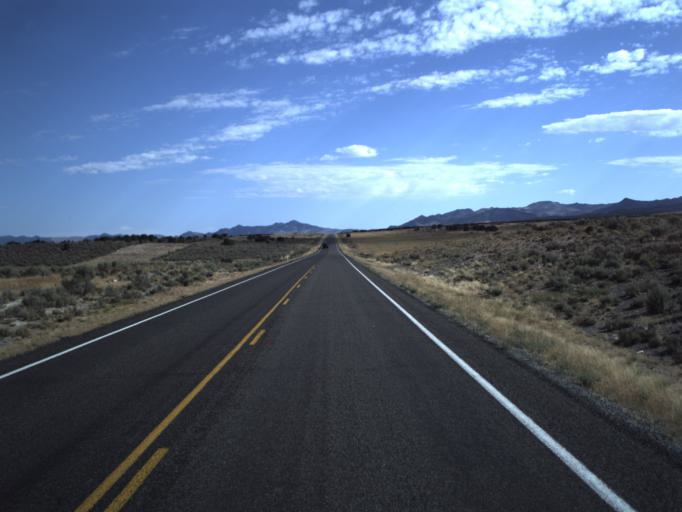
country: US
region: Utah
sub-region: Juab County
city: Mona
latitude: 39.7253
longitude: -112.1965
